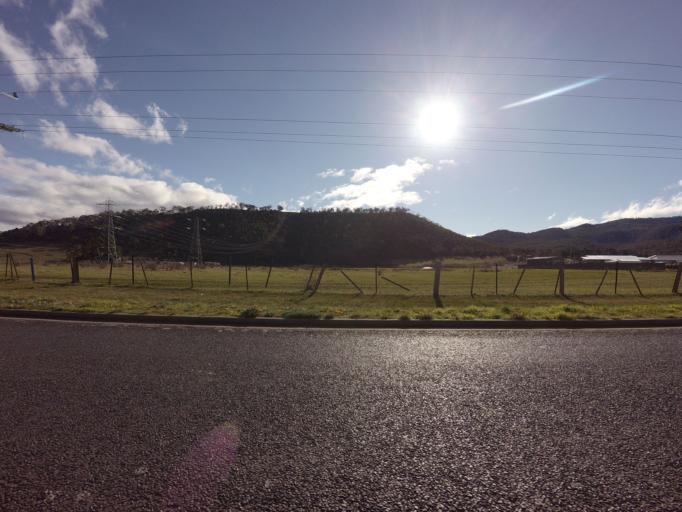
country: AU
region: Tasmania
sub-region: Derwent Valley
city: New Norfolk
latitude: -42.7583
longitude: 147.0480
